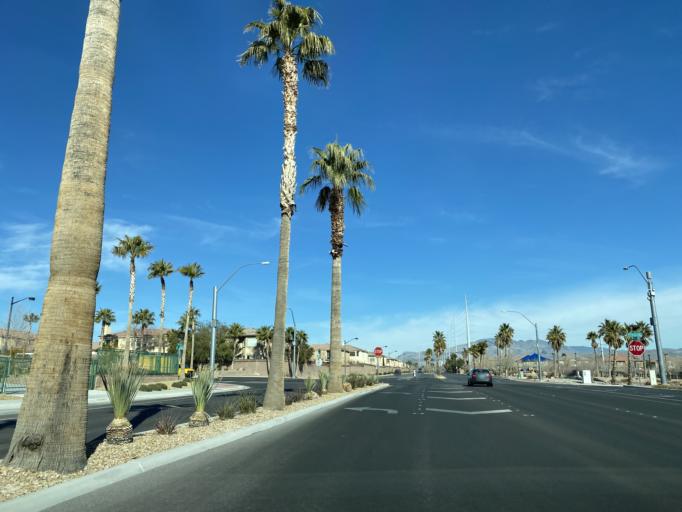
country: US
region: Nevada
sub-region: Clark County
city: Summerlin South
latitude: 36.2912
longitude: -115.2969
